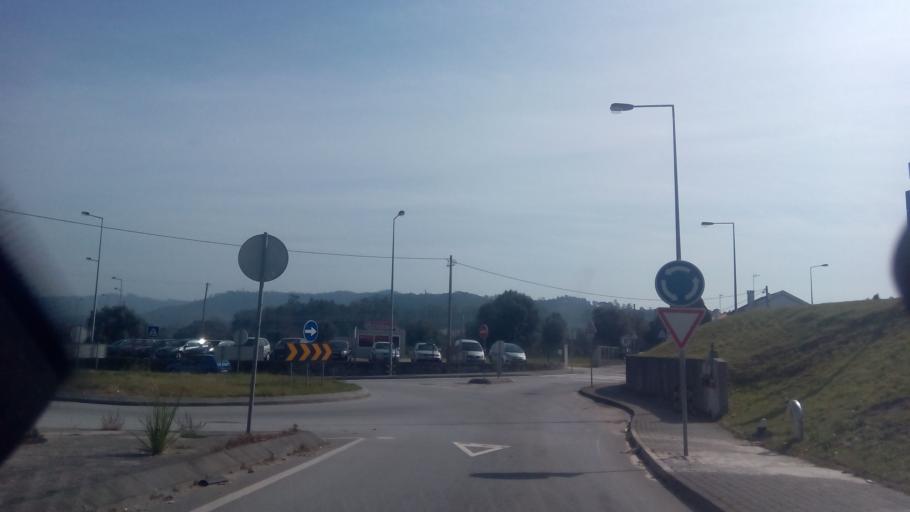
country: PT
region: Viana do Castelo
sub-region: Viana do Castelo
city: Darque
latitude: 41.6809
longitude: -8.7670
